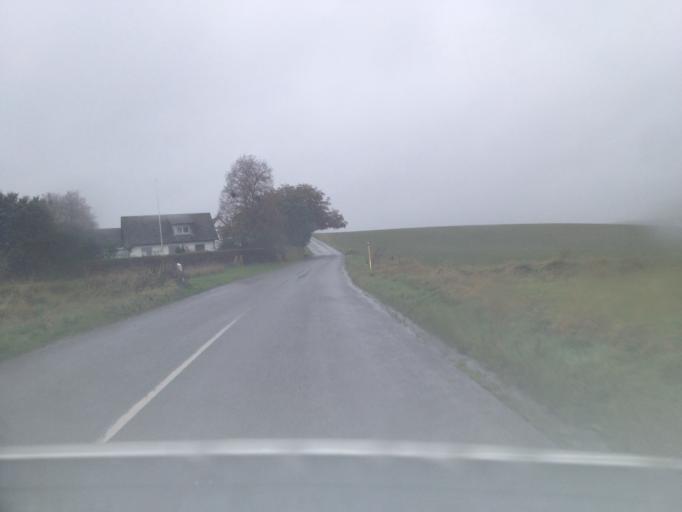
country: DK
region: Zealand
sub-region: Ringsted Kommune
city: Ringsted
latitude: 55.4860
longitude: 11.8738
